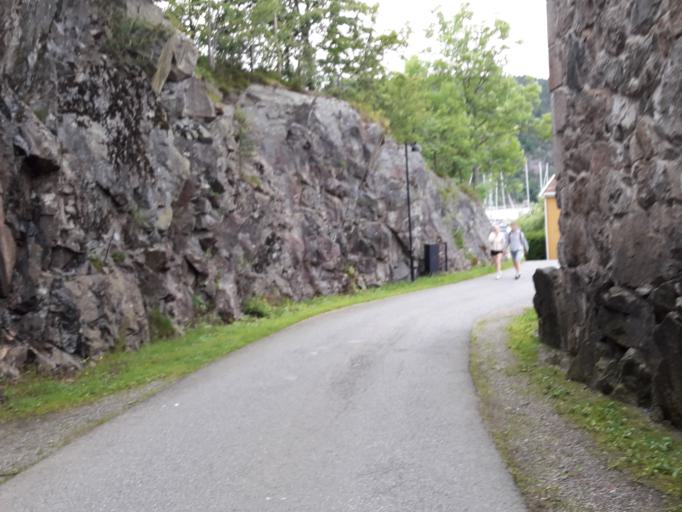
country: NO
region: Akershus
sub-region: Frogn
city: Drobak
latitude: 59.6759
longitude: 10.6070
